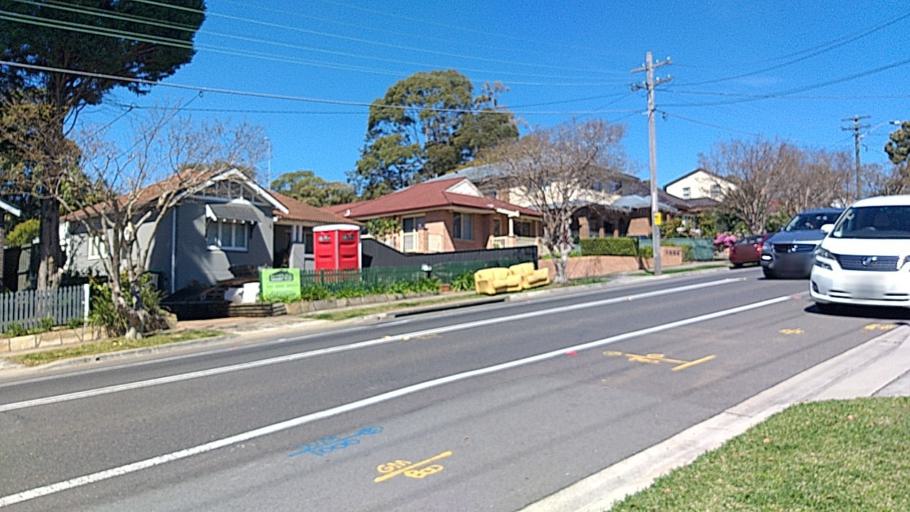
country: AU
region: New South Wales
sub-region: Ryde
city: East Ryde
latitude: -33.8212
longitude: 151.1263
